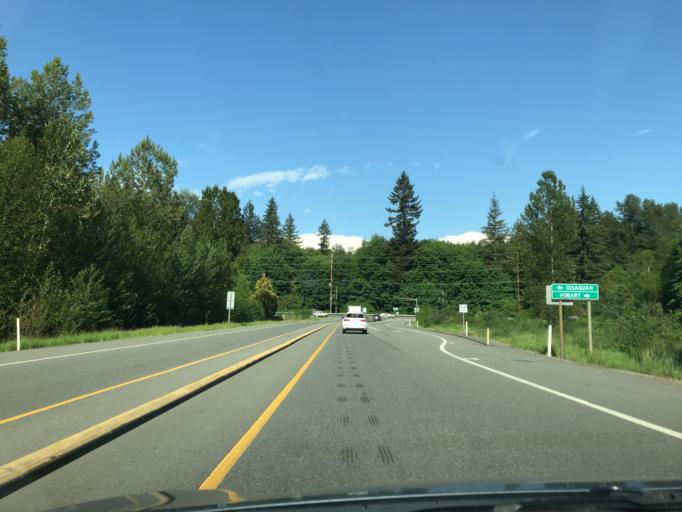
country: US
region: Washington
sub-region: King County
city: Hobart
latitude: 47.4335
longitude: -121.9751
